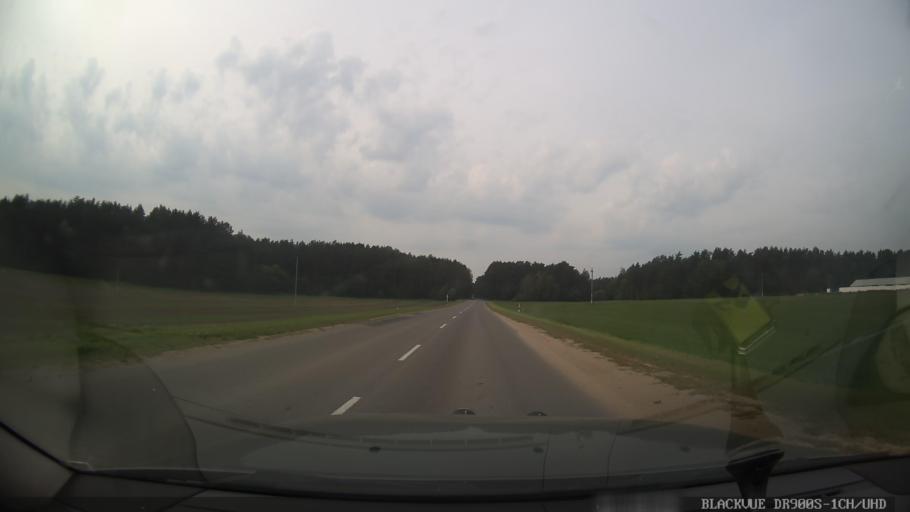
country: BY
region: Grodnenskaya
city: Astravyets
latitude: 54.6122
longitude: 26.0463
